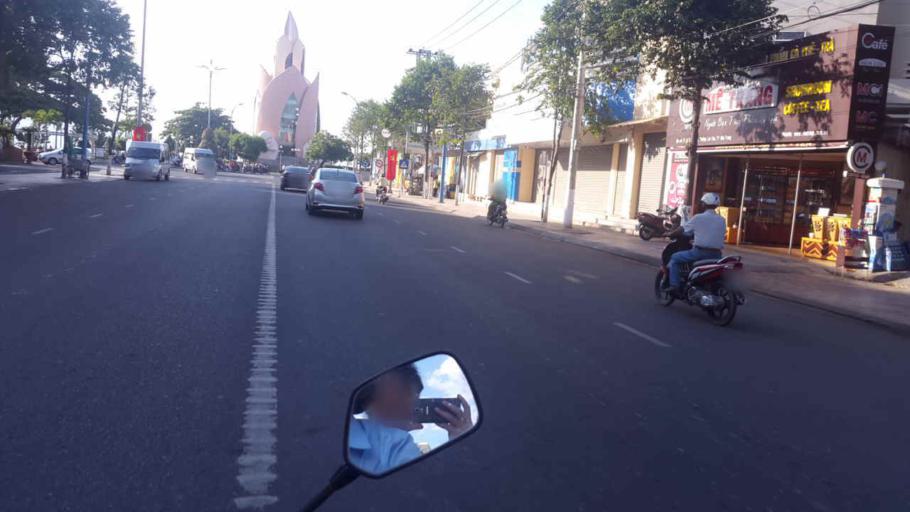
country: VN
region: Khanh Hoa
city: Nha Trang
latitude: 12.2416
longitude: 109.1957
